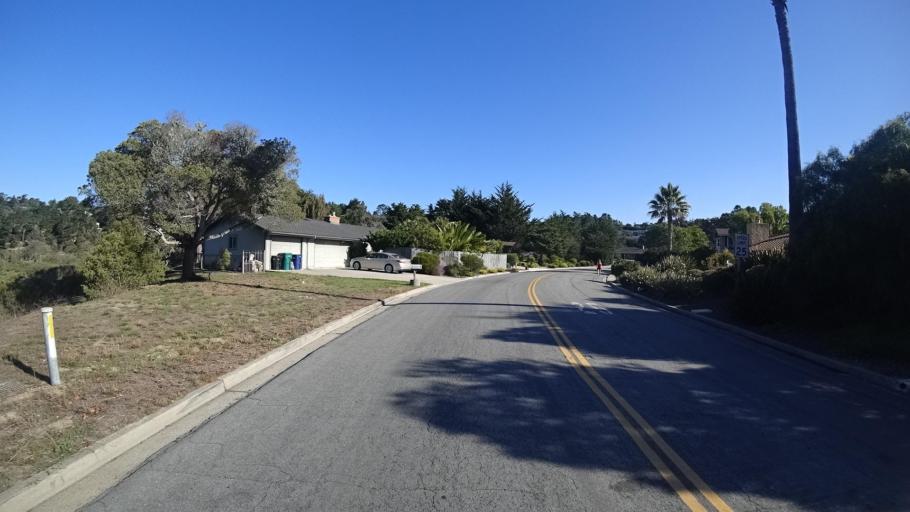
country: US
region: California
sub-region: Monterey County
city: Carmel-by-the-Sea
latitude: 36.5453
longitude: -121.9056
